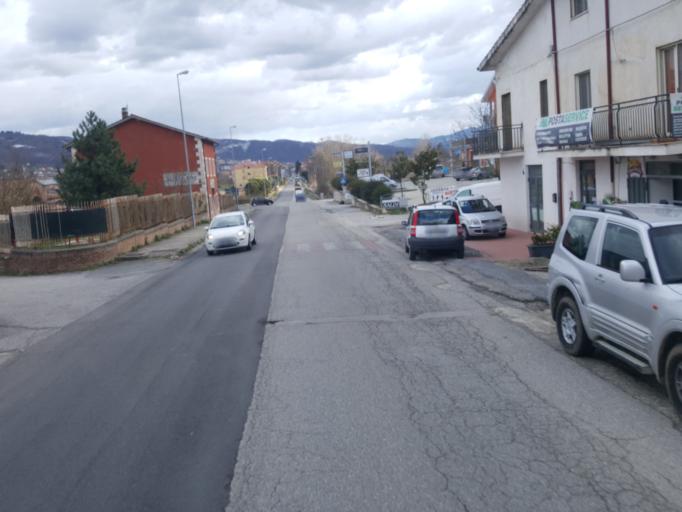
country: IT
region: Calabria
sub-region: Provincia di Cosenza
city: Santo Stefano di Rogliano
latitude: 39.2100
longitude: 16.3097
